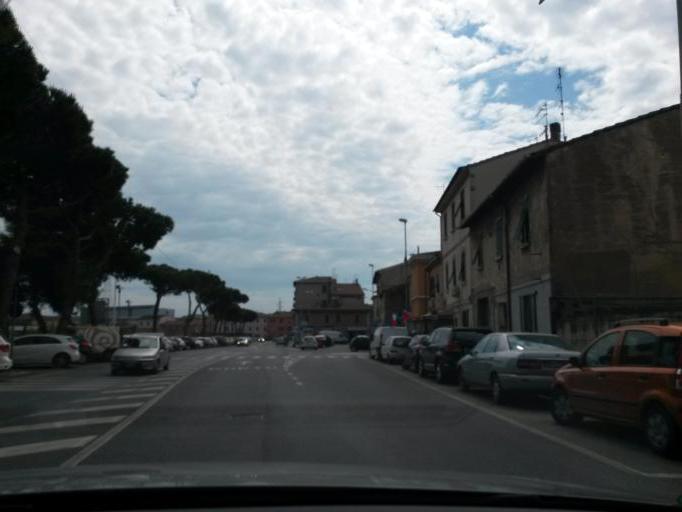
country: IT
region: Tuscany
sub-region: Provincia di Livorno
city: Piombino
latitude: 42.9285
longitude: 10.5289
